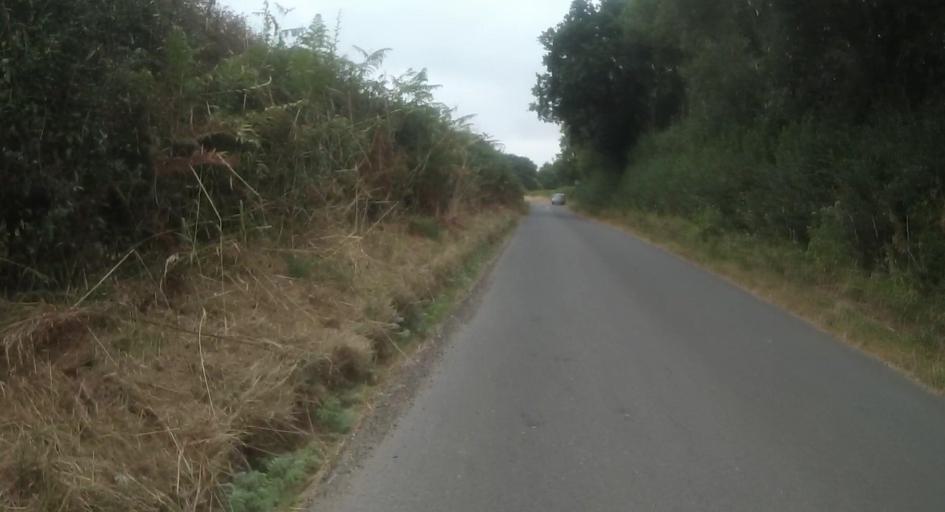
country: GB
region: England
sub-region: Dorset
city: Bovington Camp
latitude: 50.7391
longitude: -2.2185
